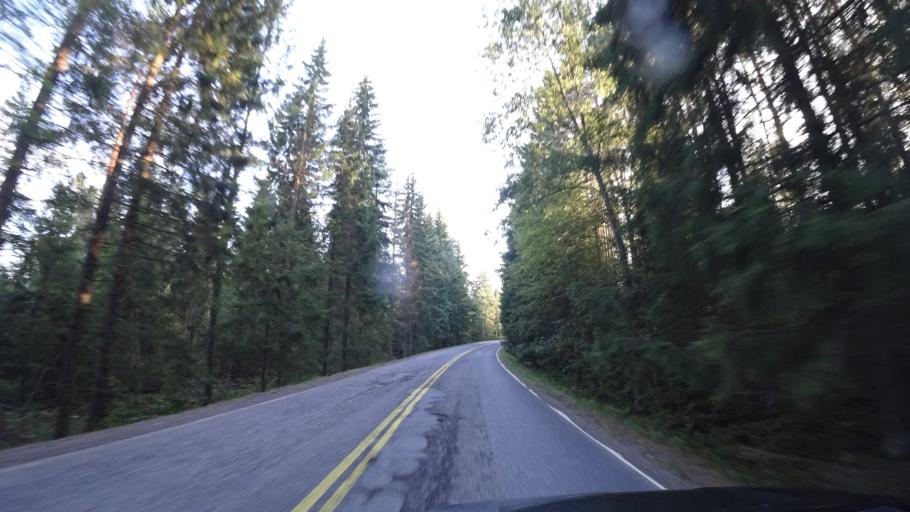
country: FI
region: Haeme
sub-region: Haemeenlinna
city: Tuulos
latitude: 61.0005
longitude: 24.8363
